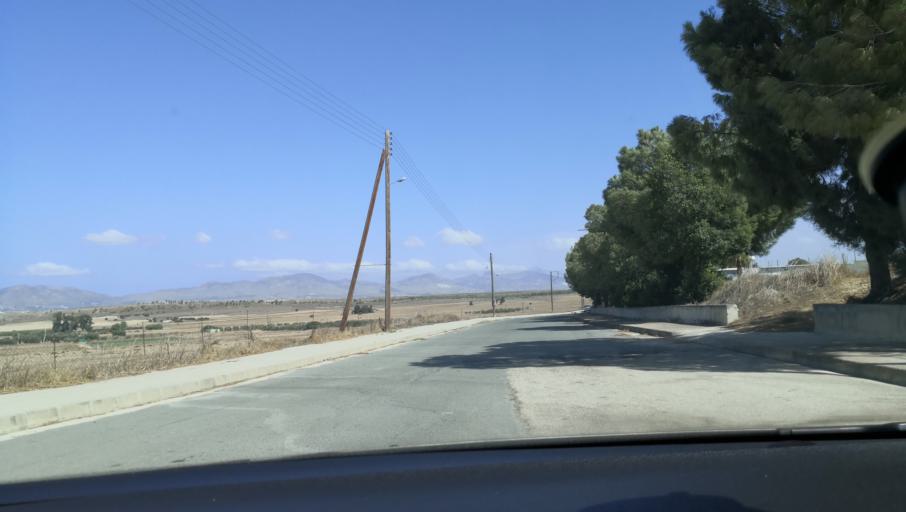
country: CY
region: Lefkosia
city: Mammari
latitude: 35.1760
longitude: 33.2086
